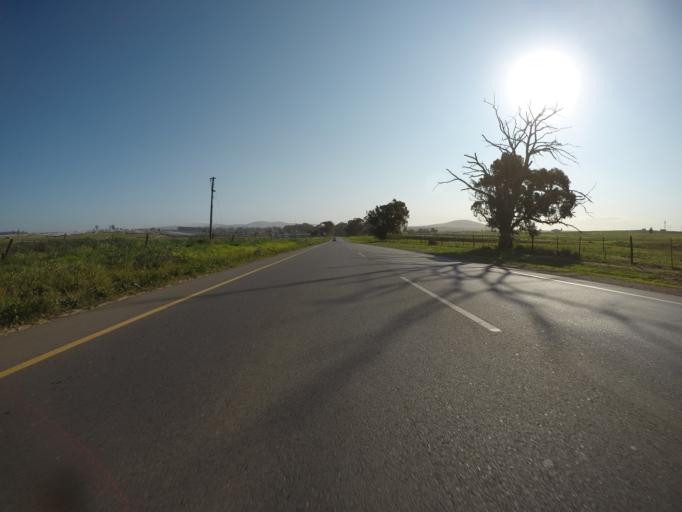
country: ZA
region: Western Cape
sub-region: City of Cape Town
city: Kraaifontein
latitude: -33.7778
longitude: 18.7279
